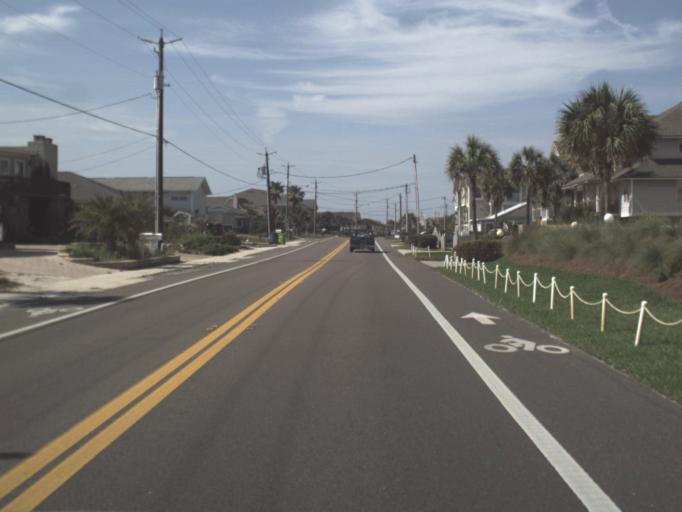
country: US
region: Florida
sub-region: Nassau County
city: Fernandina Beach
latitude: 30.6621
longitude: -81.4323
